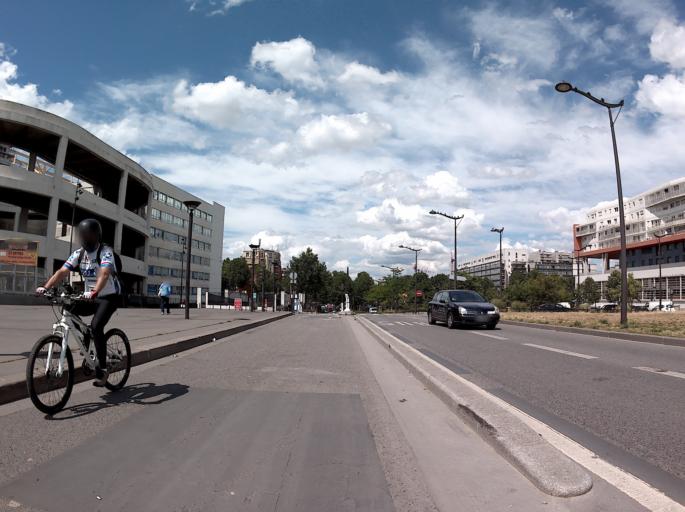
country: FR
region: Ile-de-France
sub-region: Departement de Seine-Saint-Denis
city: Aubervilliers
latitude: 48.8972
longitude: 2.3705
